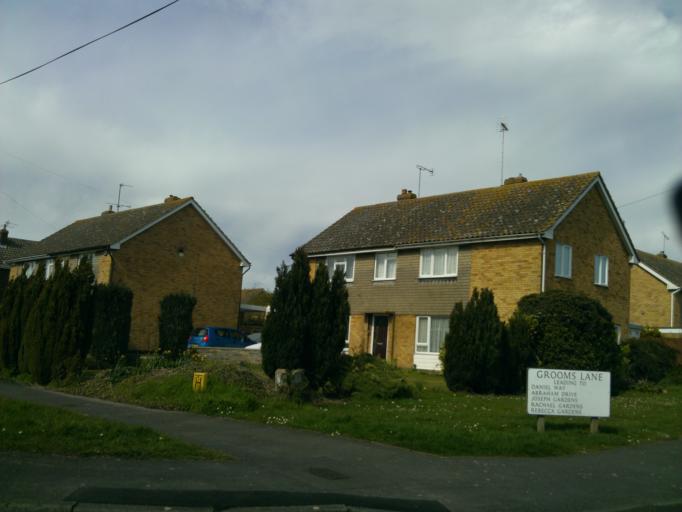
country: GB
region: England
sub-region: Essex
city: Witham
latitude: 51.8441
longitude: 0.6291
